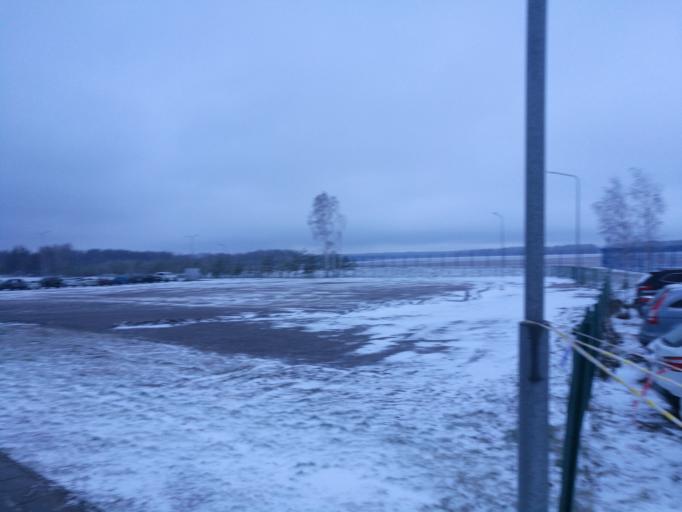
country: BY
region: Minsk
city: Horad Smalyavichy
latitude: 53.8914
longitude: 28.0377
